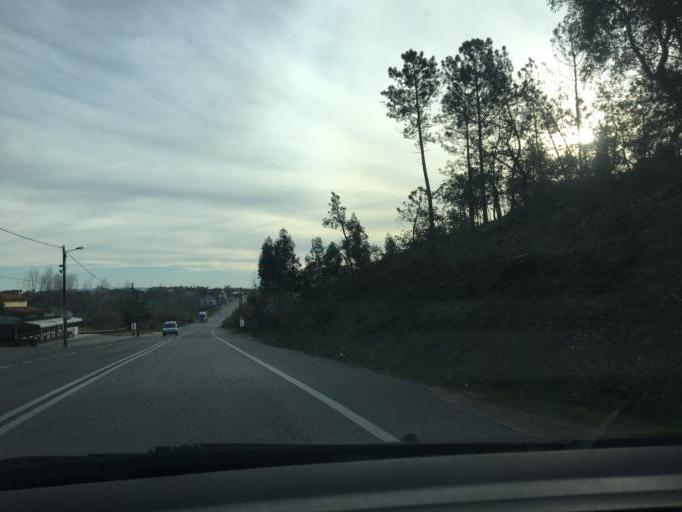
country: PT
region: Coimbra
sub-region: Montemor-O-Velho
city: Arazede
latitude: 40.2186
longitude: -8.5925
